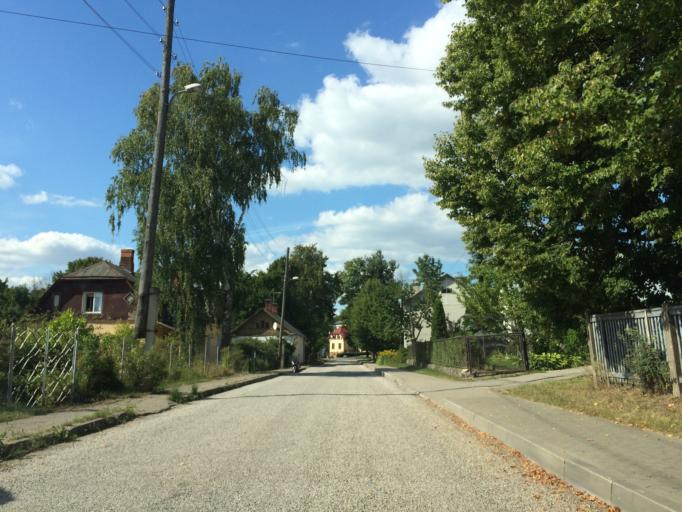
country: LV
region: Rezekne
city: Rezekne
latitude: 56.5031
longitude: 27.3377
